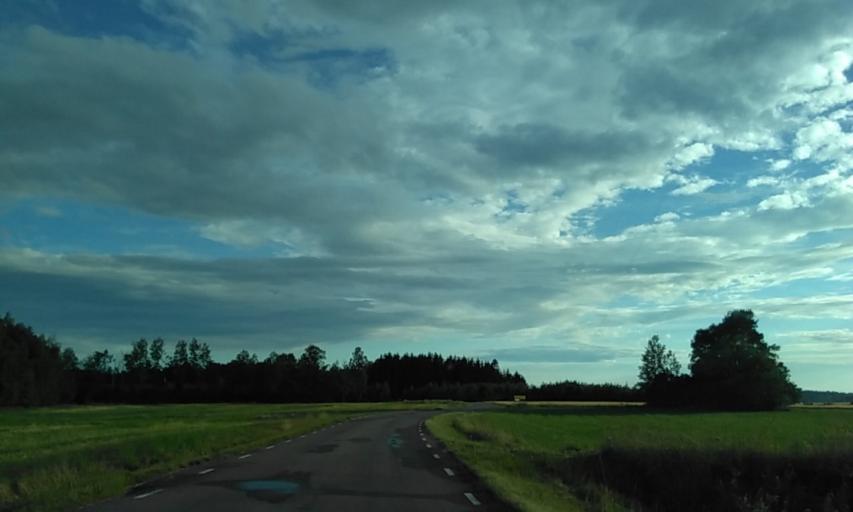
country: SE
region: Vaestra Goetaland
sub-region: Grastorps Kommun
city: Graestorp
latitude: 58.3513
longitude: 12.7791
